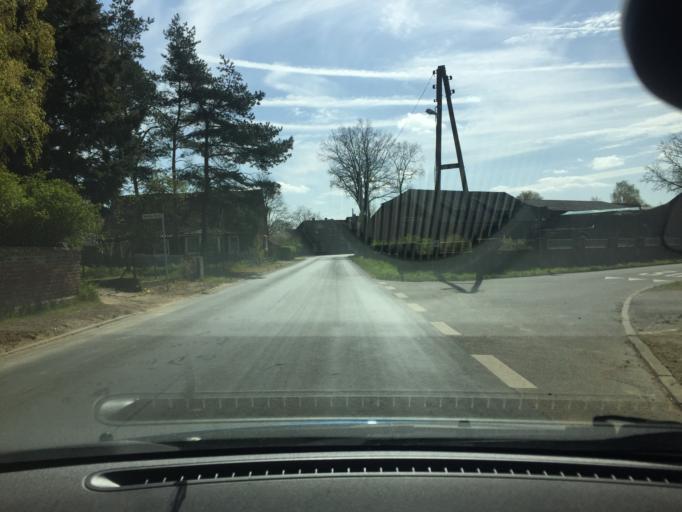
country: DE
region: Lower Saxony
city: Ratzlingen
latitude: 52.9567
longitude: 10.6689
